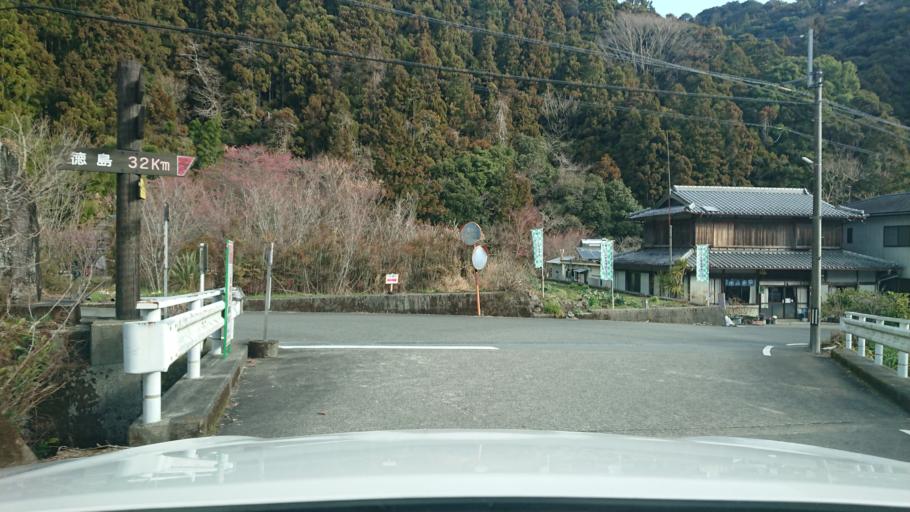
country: JP
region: Tokushima
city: Ishii
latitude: 33.9154
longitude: 134.4163
